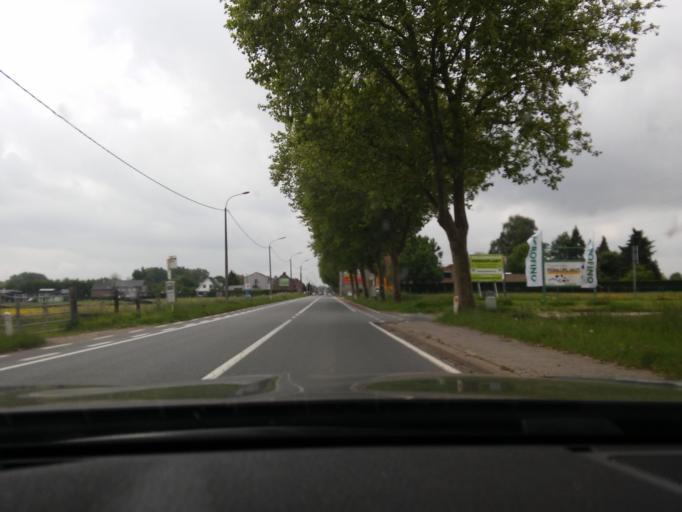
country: BE
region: Flanders
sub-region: Provincie Vlaams-Brabant
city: Ternat
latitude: 50.8596
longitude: 4.1561
